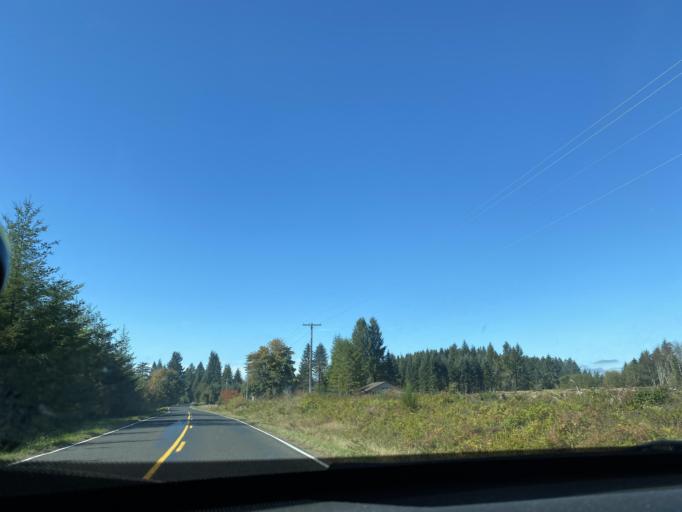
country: US
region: Washington
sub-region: Clallam County
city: Forks
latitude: 47.9484
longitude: -124.5116
